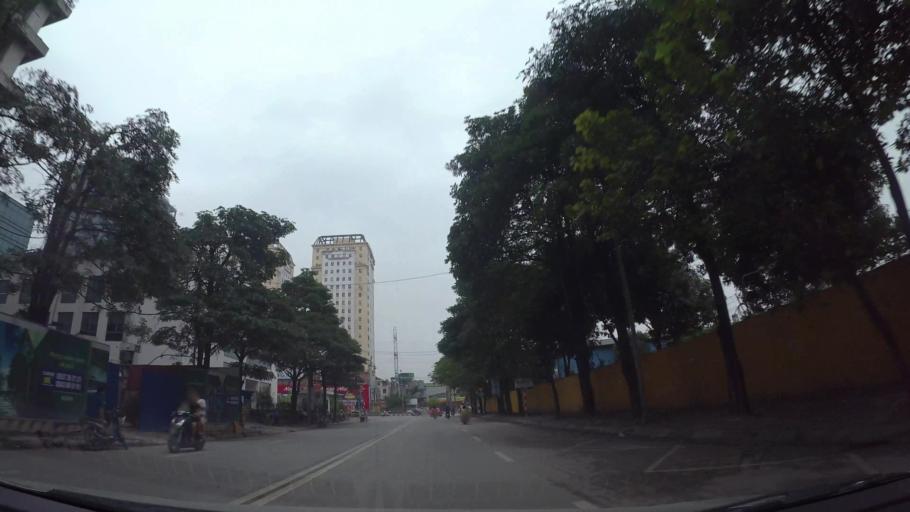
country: VN
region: Ha Noi
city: Cau Dien
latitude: 21.0313
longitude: 105.7810
